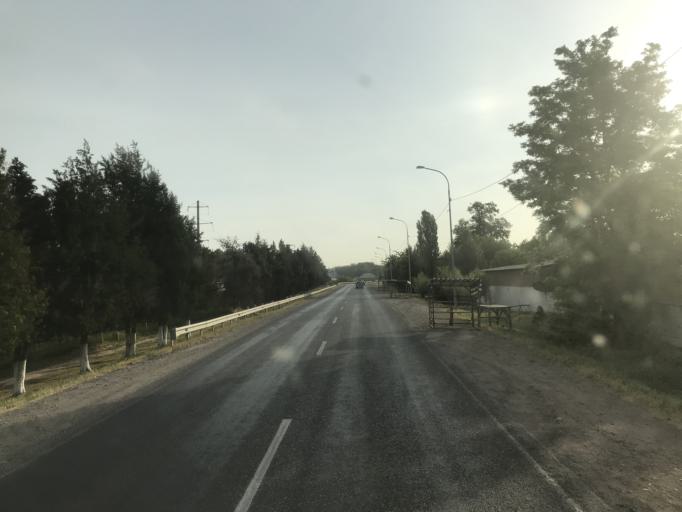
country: KZ
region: Ongtustik Qazaqstan
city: Saryaghash
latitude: 41.4875
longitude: 69.2575
